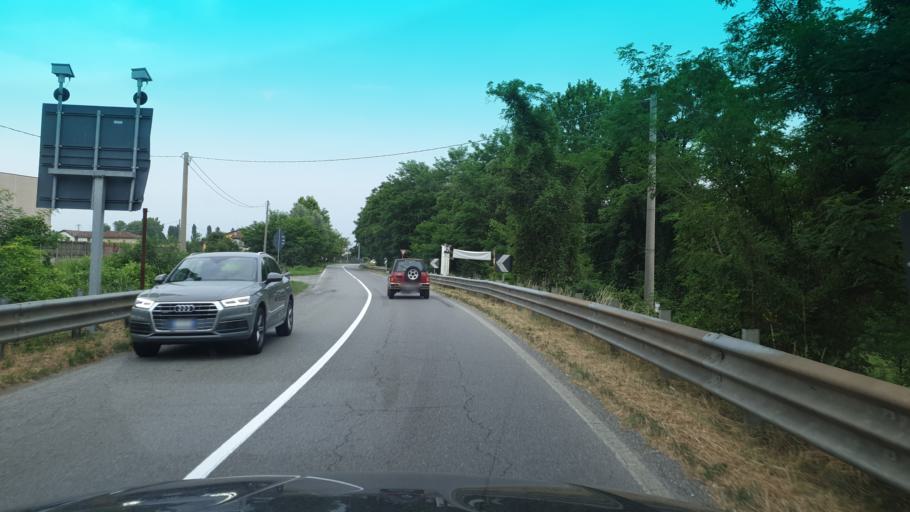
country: IT
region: Lombardy
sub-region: Provincia di Bergamo
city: Badalasco
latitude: 45.5361
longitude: 9.5372
